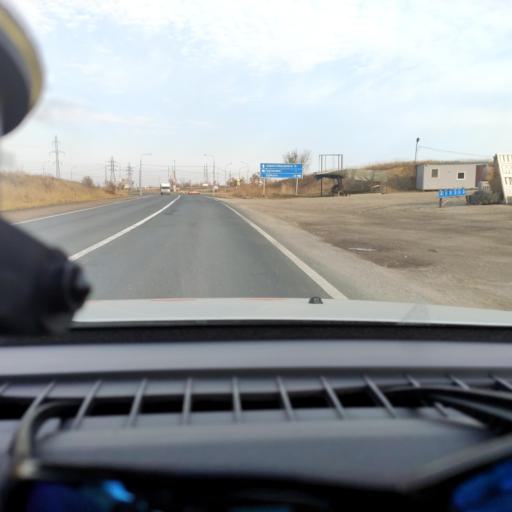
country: RU
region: Samara
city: Chapayevsk
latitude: 52.9952
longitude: 49.7683
